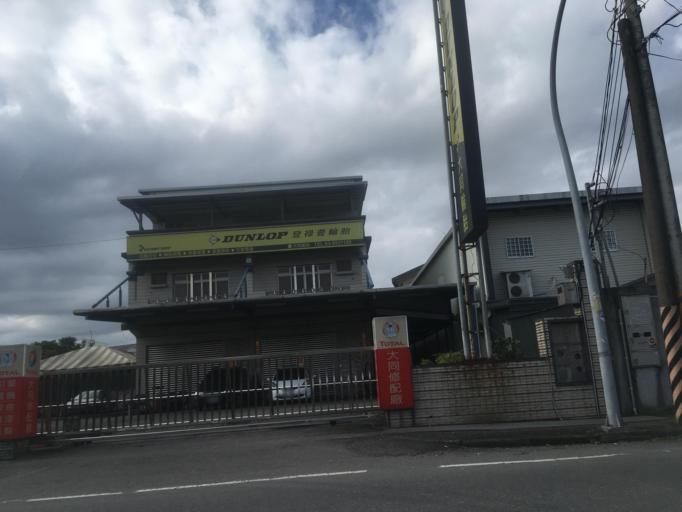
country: TW
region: Taiwan
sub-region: Yilan
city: Yilan
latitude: 24.6872
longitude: 121.7394
